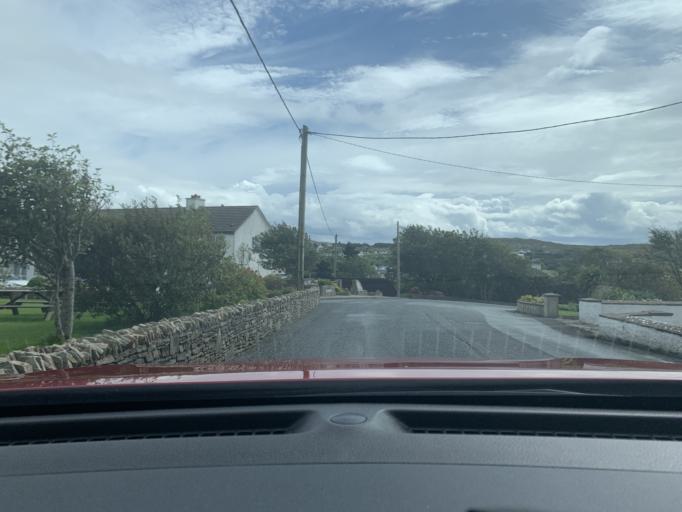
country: IE
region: Ulster
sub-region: County Donegal
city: Dungloe
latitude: 54.9527
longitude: -8.3632
